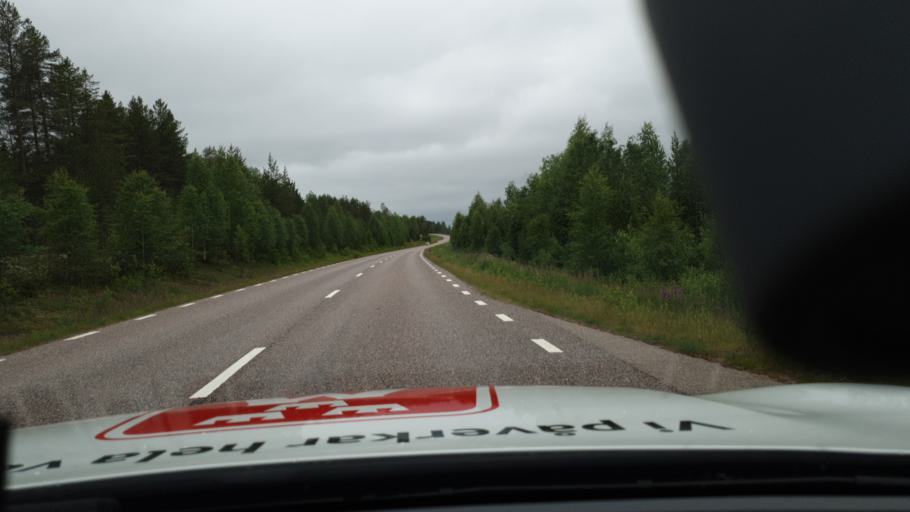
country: FI
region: Lapland
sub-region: Tunturi-Lappi
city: Kolari
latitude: 67.0256
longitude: 23.7214
